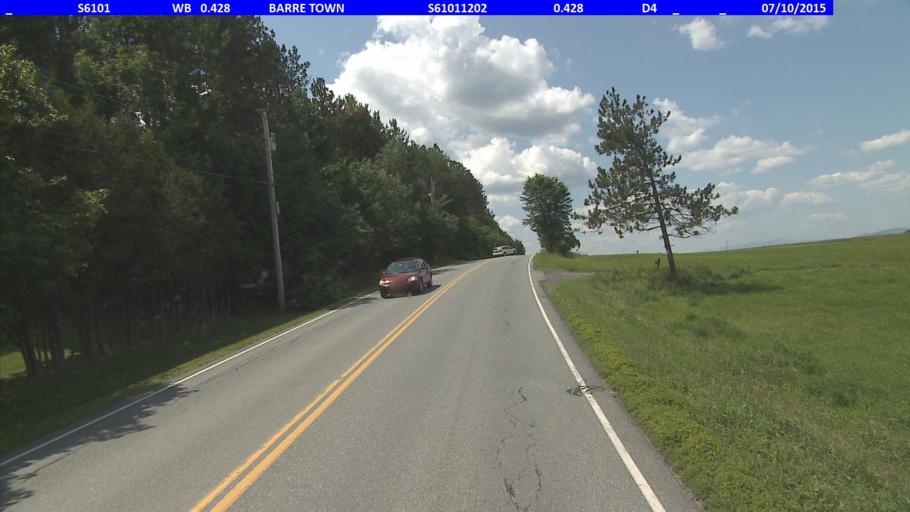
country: US
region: Vermont
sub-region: Washington County
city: South Barre
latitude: 44.1879
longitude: -72.5380
